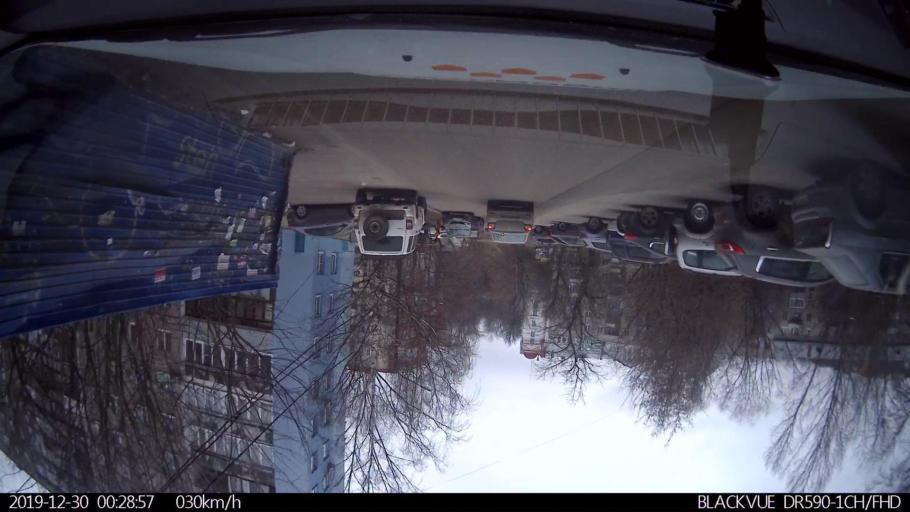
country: RU
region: Nizjnij Novgorod
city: Nizhniy Novgorod
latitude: 56.3209
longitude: 44.0253
